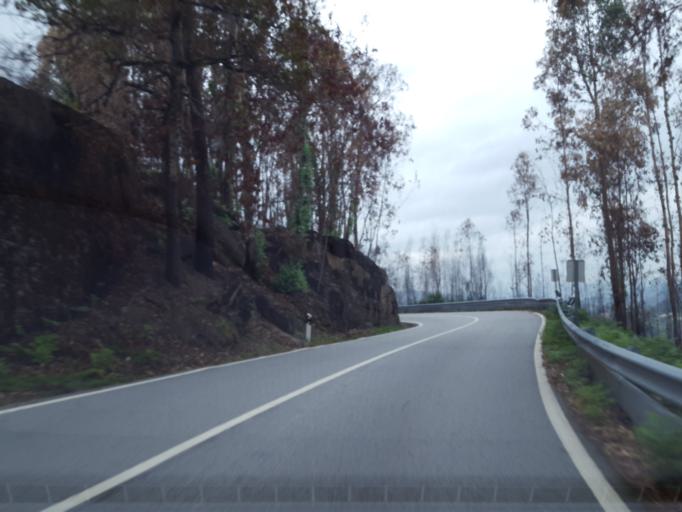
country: PT
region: Porto
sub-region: Marco de Canaveses
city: Marco de Canavezes
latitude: 41.1508
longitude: -8.1330
